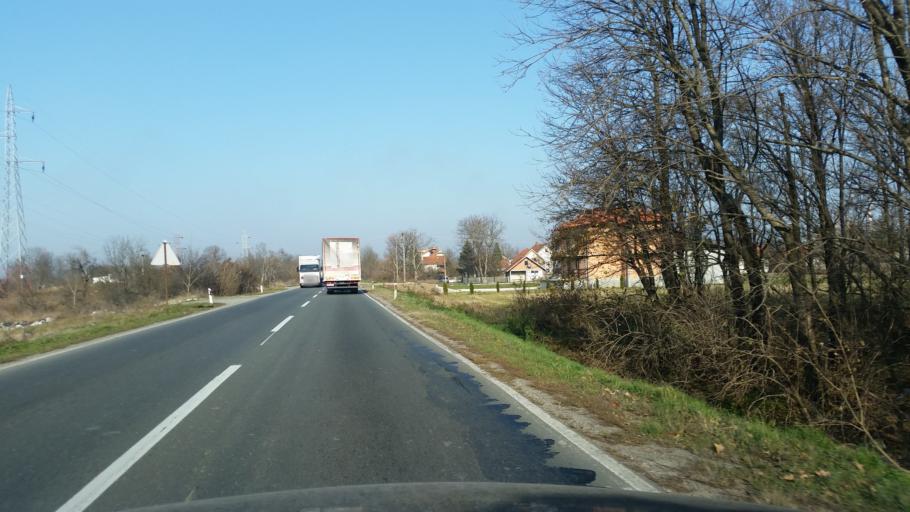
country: RS
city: Stepojevac
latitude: 44.4698
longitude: 20.2757
